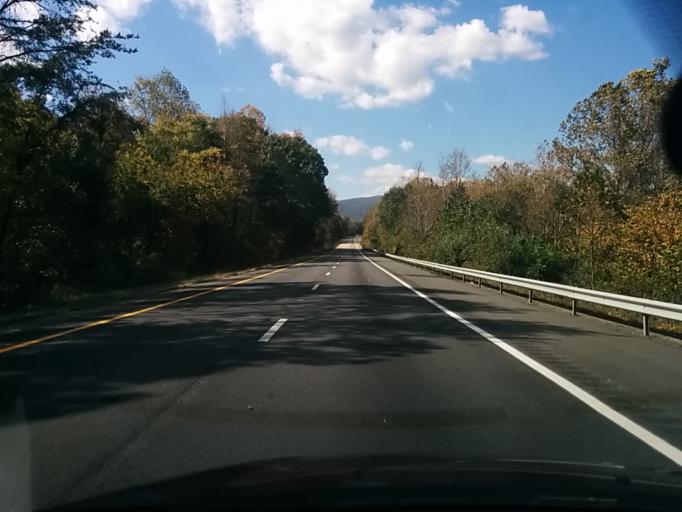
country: US
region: Virginia
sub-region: Albemarle County
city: Crozet
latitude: 38.0387
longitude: -78.7076
